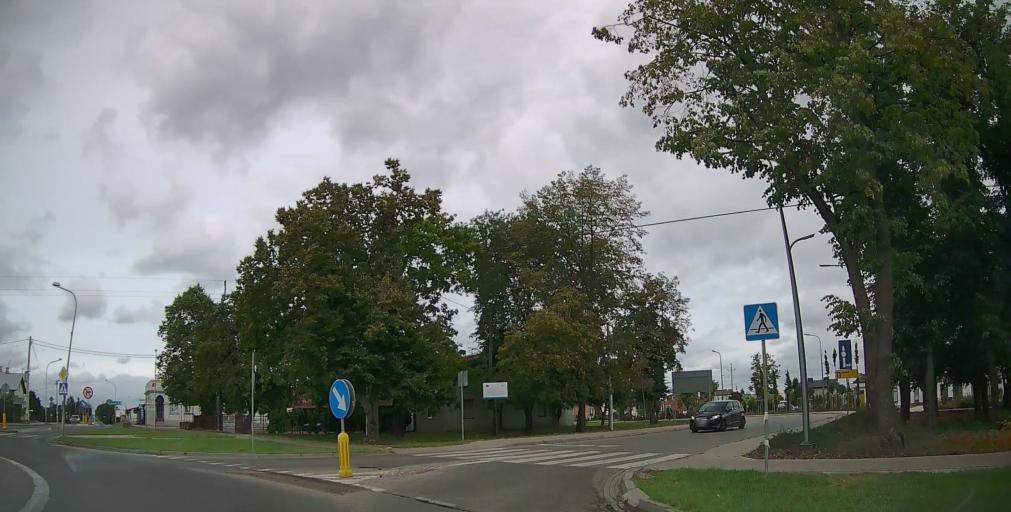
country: PL
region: Masovian Voivodeship
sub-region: Powiat grojecki
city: Belsk Duzy
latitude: 51.8247
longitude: 20.8083
